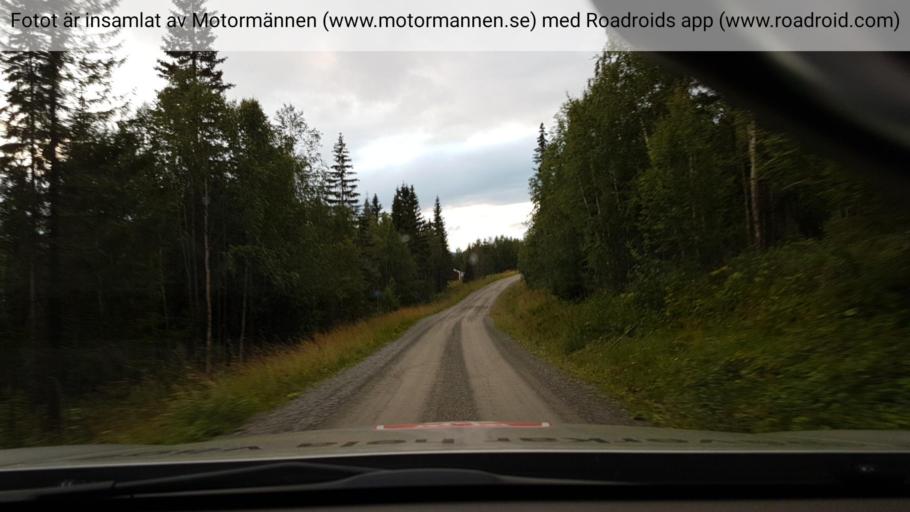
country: NO
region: Nordland
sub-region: Hattfjelldal
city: Hattfjelldal
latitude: 65.6161
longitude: 15.2516
